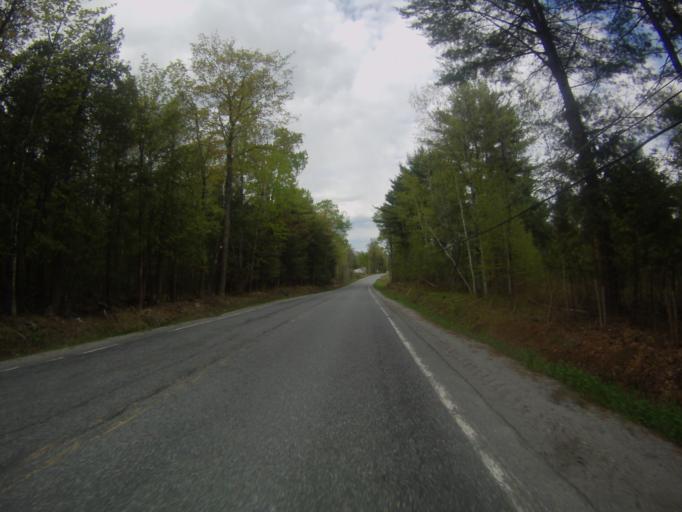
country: US
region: New York
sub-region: Essex County
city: Port Henry
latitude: 44.0106
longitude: -73.5000
